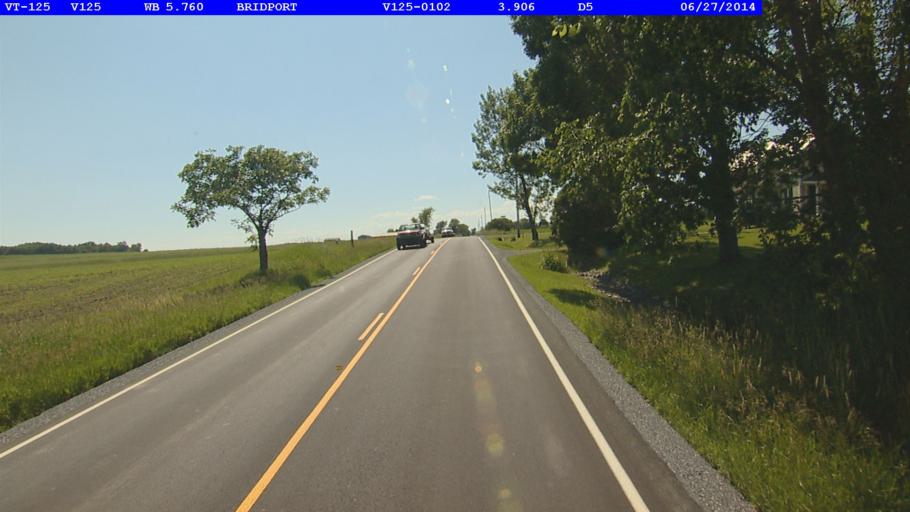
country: US
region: New York
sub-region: Essex County
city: Port Henry
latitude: 43.9918
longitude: -73.3377
